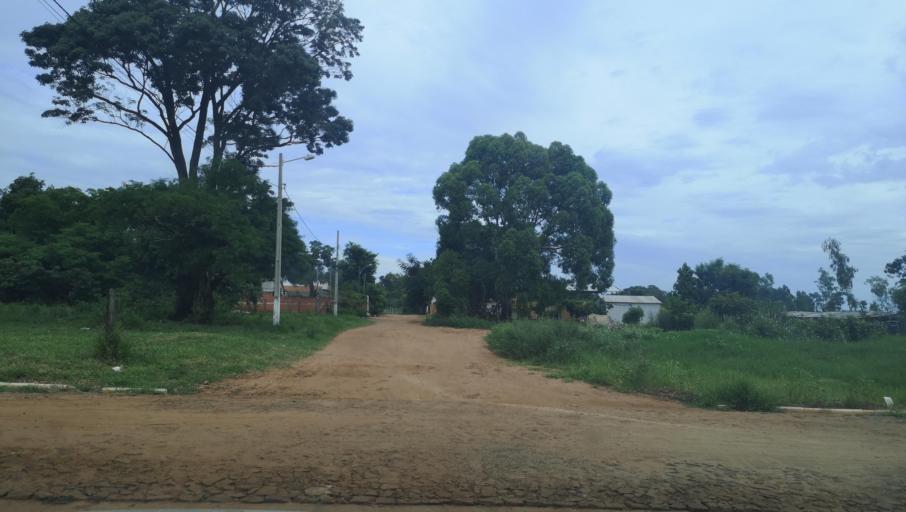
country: PY
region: San Pedro
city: Capiibary
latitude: -24.7390
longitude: -56.0252
